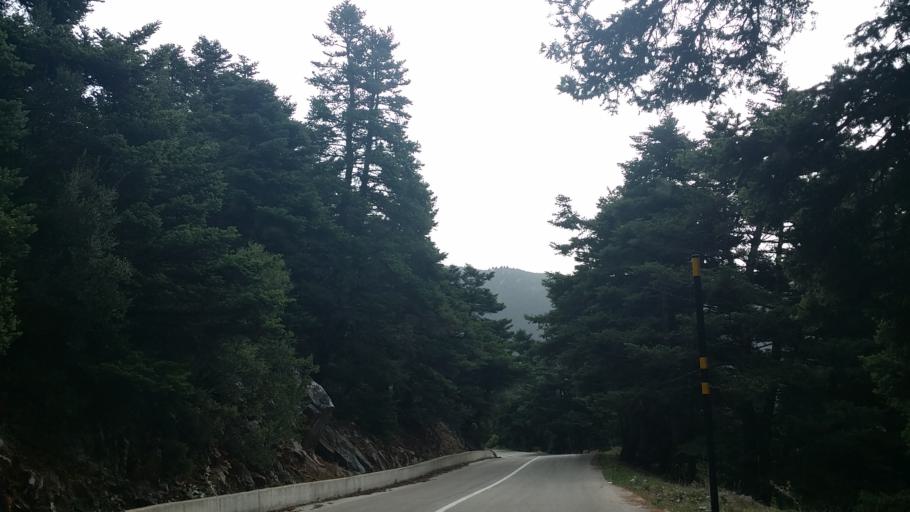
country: GR
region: Central Greece
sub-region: Nomos Voiotias
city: Kyriaki
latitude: 38.3821
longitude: 22.8383
